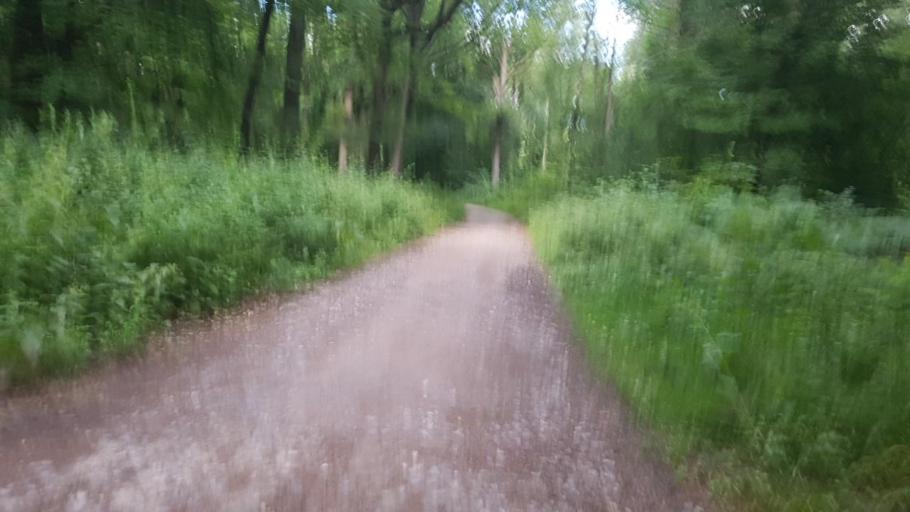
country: BE
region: Wallonia
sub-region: Province du Hainaut
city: Charleroi
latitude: 50.3567
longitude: 4.4444
